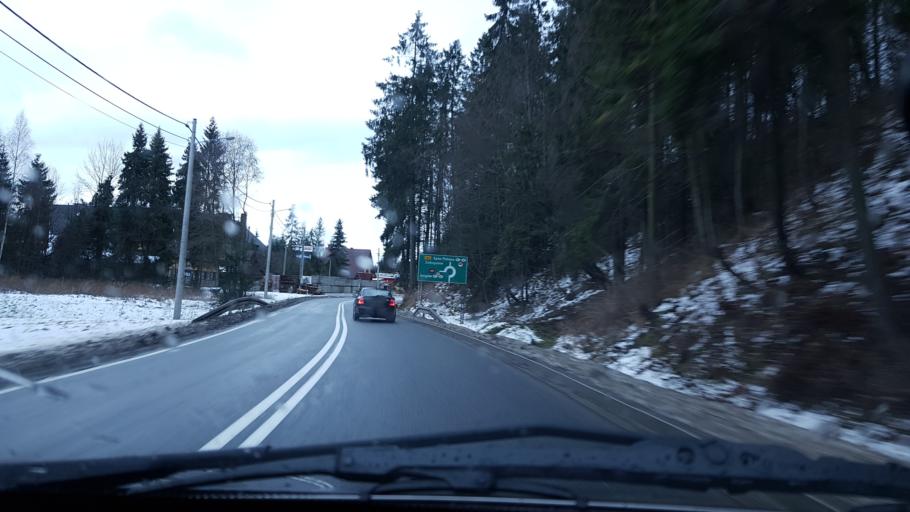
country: PL
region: Lesser Poland Voivodeship
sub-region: Powiat tatrzanski
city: Czarna Gora
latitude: 49.3588
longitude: 20.1223
